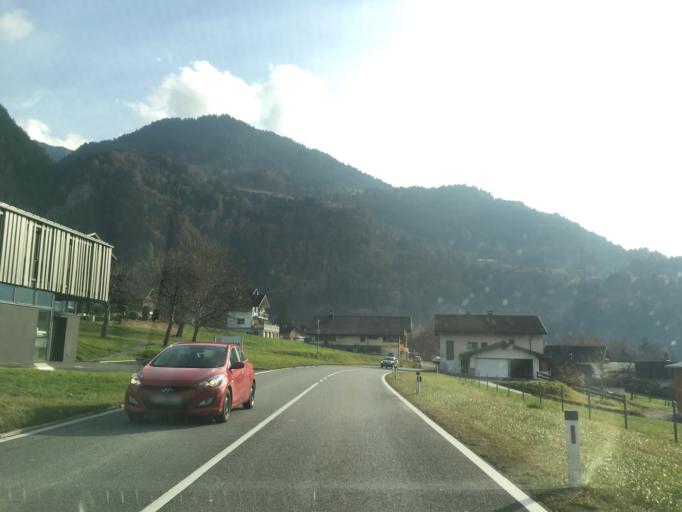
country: AT
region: Vorarlberg
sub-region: Politischer Bezirk Bludenz
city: Sankt Anton im Montafon
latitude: 47.1144
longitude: 9.8630
